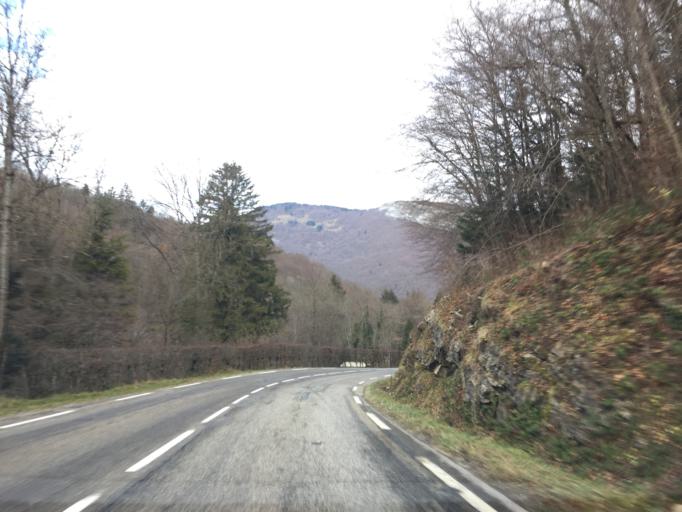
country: FR
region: Rhone-Alpes
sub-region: Departement de la Haute-Savoie
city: Gruffy
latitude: 45.7290
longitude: 6.0952
